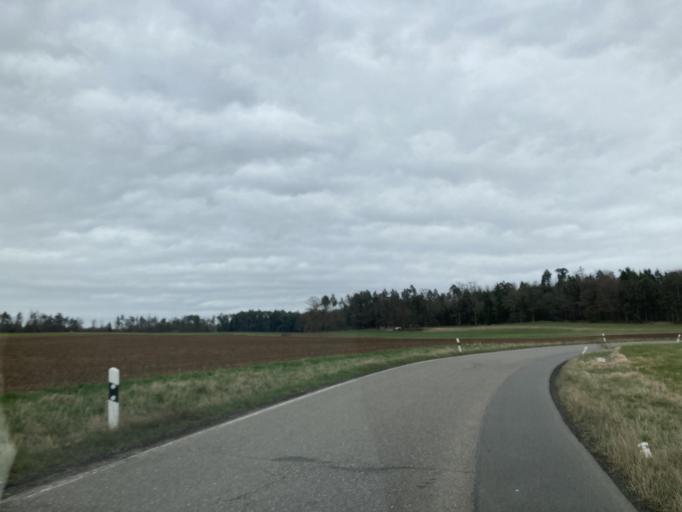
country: DE
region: Baden-Wuerttemberg
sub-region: Tuebingen Region
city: Rottenburg
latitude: 48.5049
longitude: 8.8944
